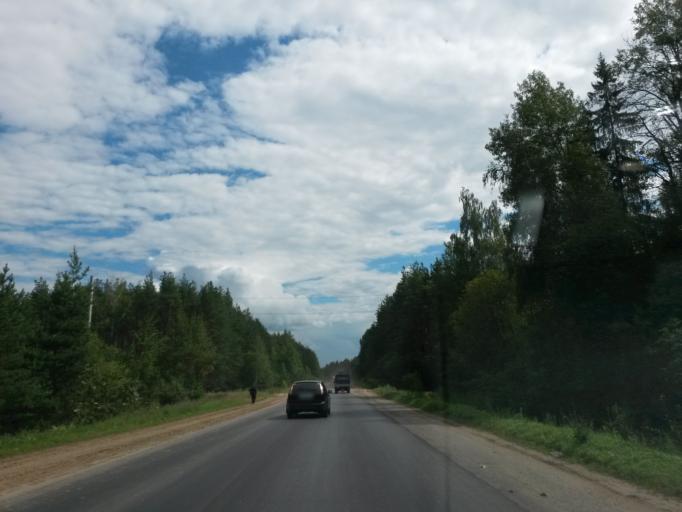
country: RU
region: Ivanovo
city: Novo-Talitsy
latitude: 57.0192
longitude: 40.7778
